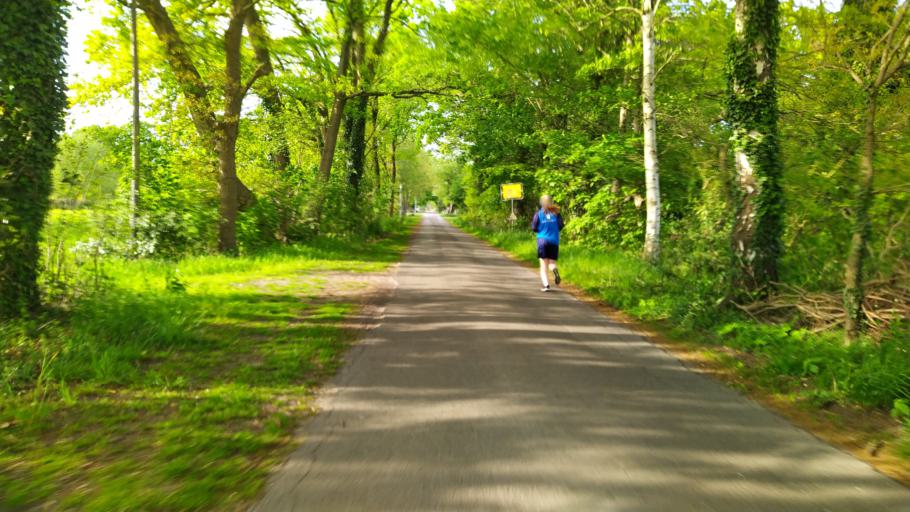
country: DE
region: Lower Saxony
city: Farven
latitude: 53.4282
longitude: 9.3490
